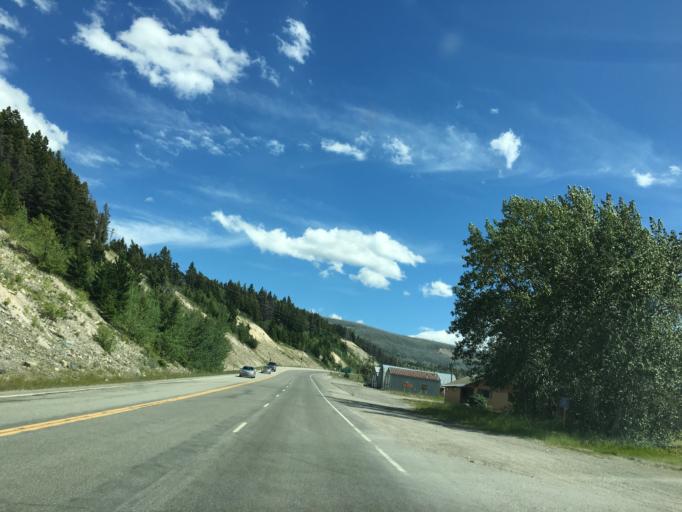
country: US
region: Montana
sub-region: Glacier County
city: North Browning
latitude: 48.7408
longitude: -113.4284
